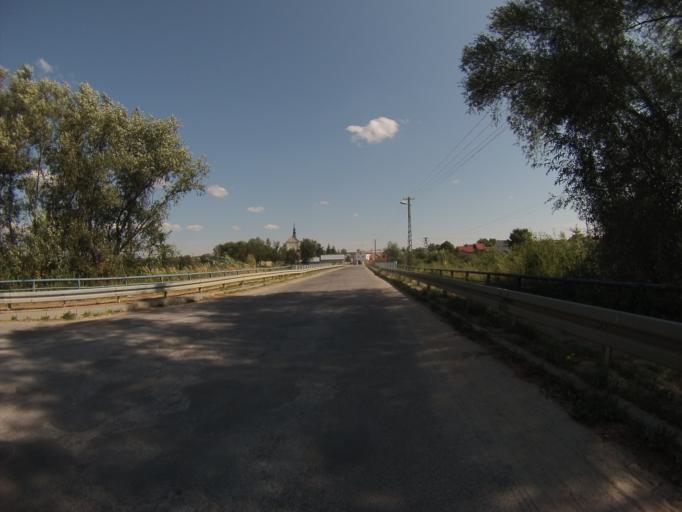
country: PL
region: Swietokrzyskie
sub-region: Powiat kielecki
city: Rakow
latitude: 50.6729
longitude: 21.0384
